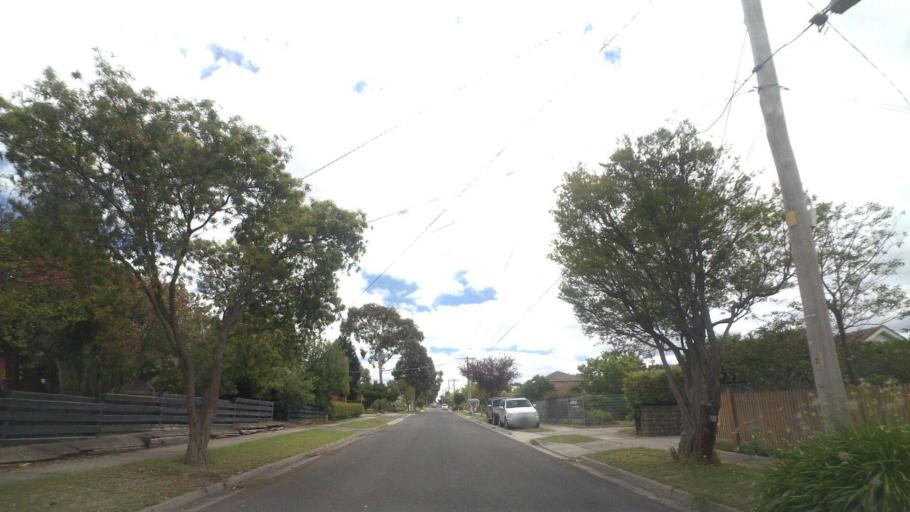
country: AU
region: Victoria
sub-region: Knox
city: Bayswater
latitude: -37.8577
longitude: 145.2474
